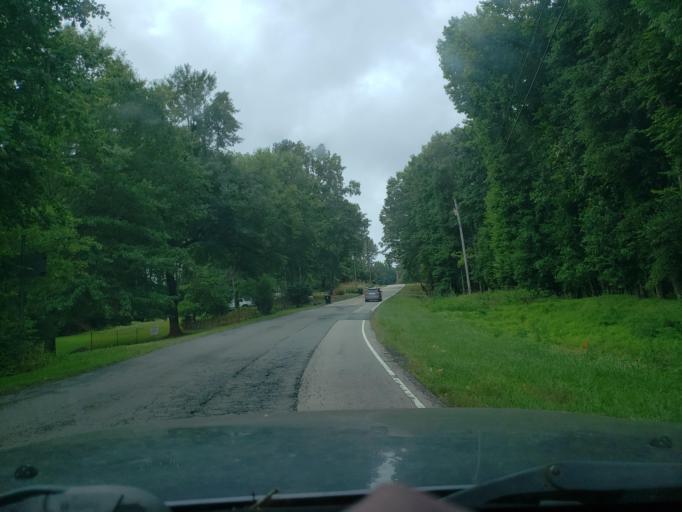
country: US
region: North Carolina
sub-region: Durham County
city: Gorman
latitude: 35.9662
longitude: -78.7830
